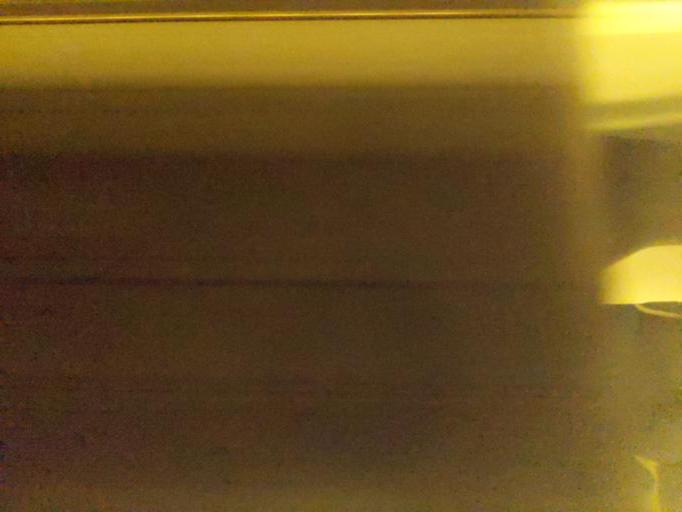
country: JP
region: Gifu
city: Tarui
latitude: 35.3597
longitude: 136.4334
